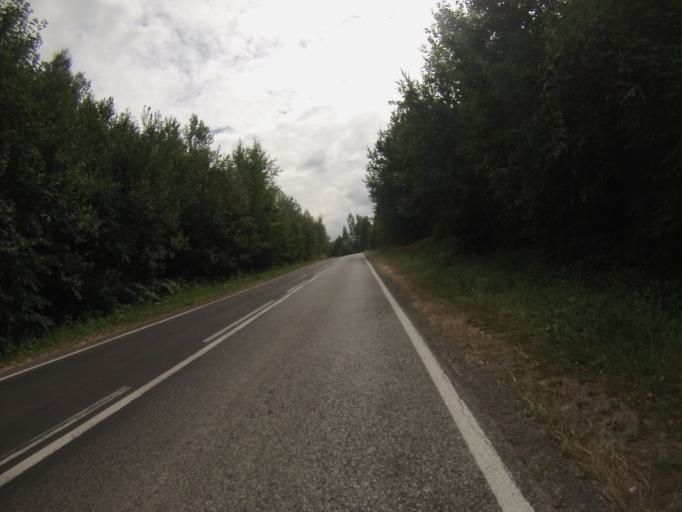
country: PL
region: Swietokrzyskie
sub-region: Powiat kielecki
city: Lagow
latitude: 50.7416
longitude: 21.0711
